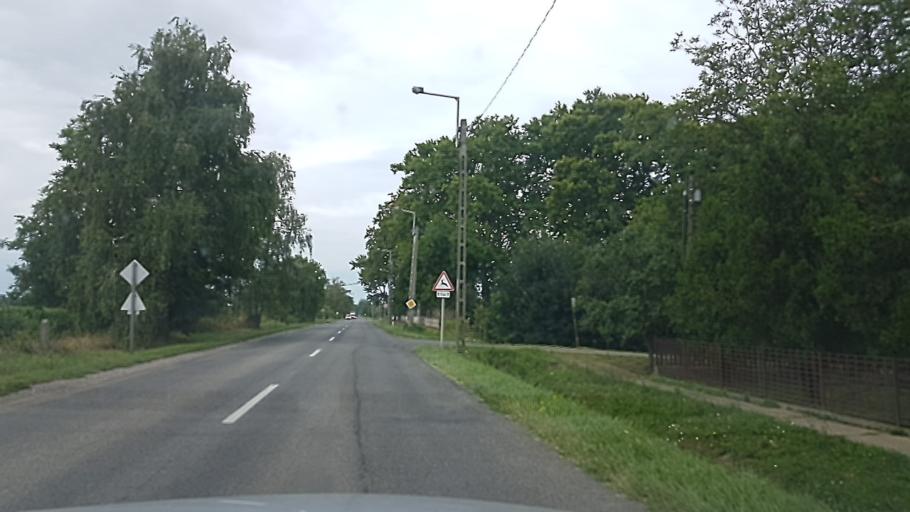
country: HU
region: Baranya
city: Szigetvar
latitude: 46.0406
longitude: 17.7390
